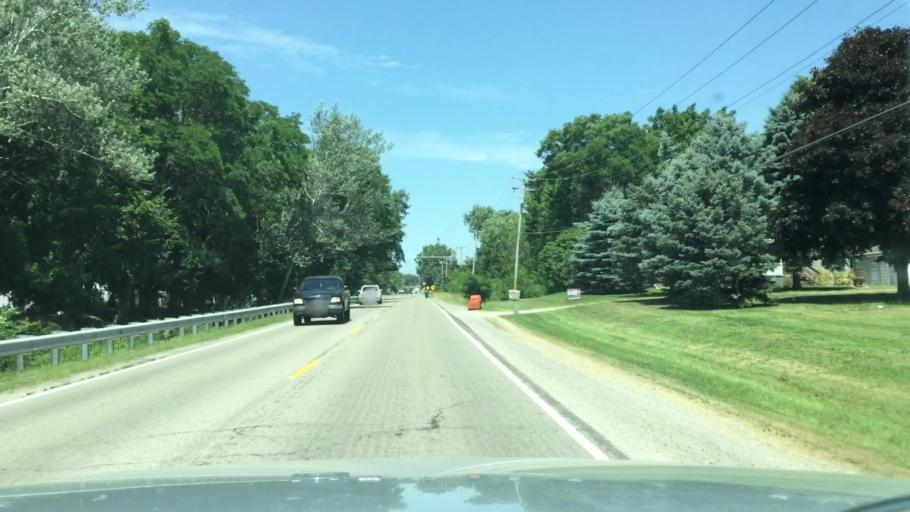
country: US
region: Michigan
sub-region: Genesee County
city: Swartz Creek
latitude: 42.9551
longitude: -83.8110
